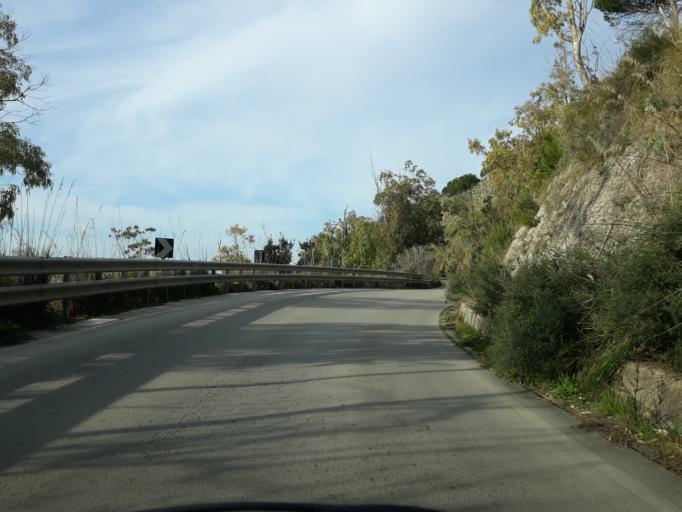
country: IT
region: Sicily
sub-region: Palermo
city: Torretta
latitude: 38.1145
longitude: 13.2417
